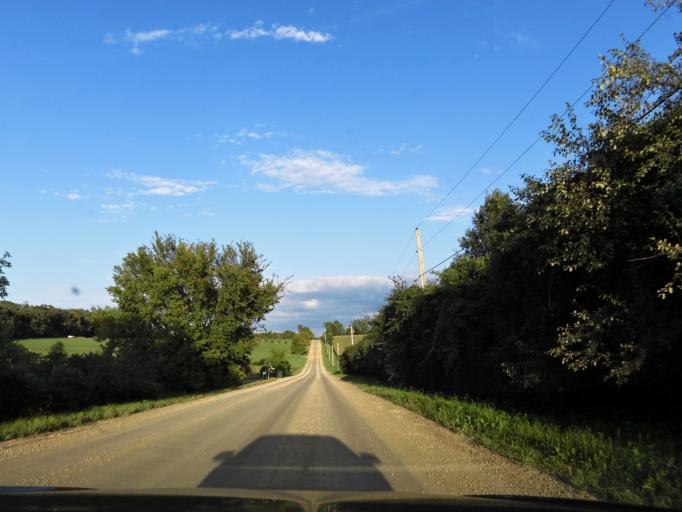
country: US
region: Minnesota
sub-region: Washington County
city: Cottage Grove
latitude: 44.8765
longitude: -92.8789
